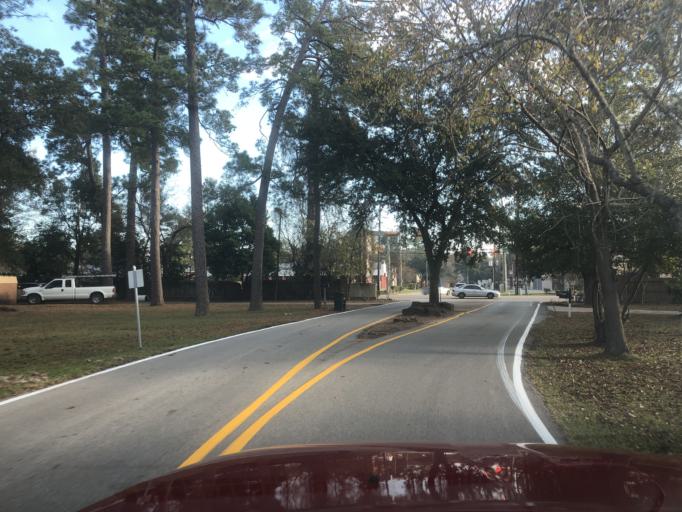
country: US
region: Texas
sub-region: Harris County
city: Spring
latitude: 30.0140
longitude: -95.4699
